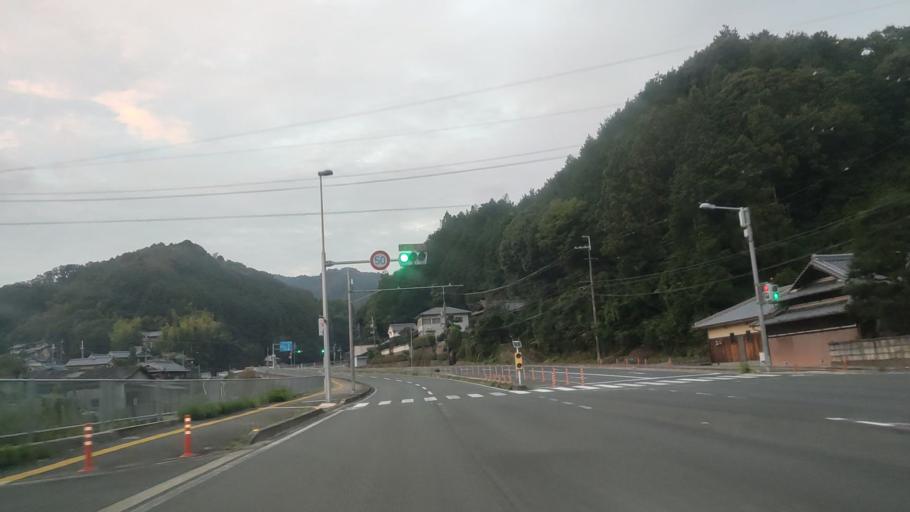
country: JP
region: Wakayama
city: Hashimoto
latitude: 34.3608
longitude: 135.6064
